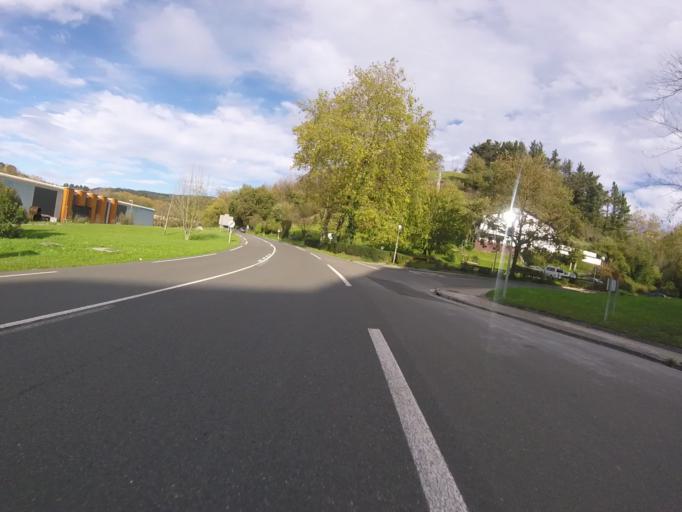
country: ES
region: Basque Country
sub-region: Provincia de Guipuzcoa
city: Usurbil
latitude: 43.2733
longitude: -2.0539
